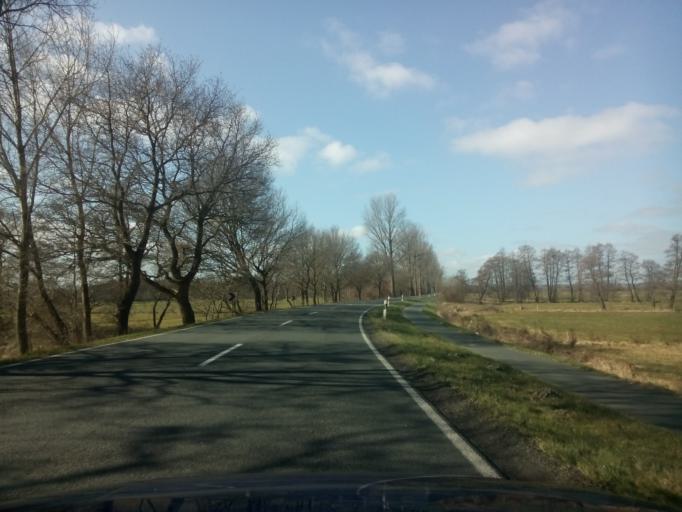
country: DE
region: Lower Saxony
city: Osterholz-Scharmbeck
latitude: 53.1921
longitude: 8.8328
